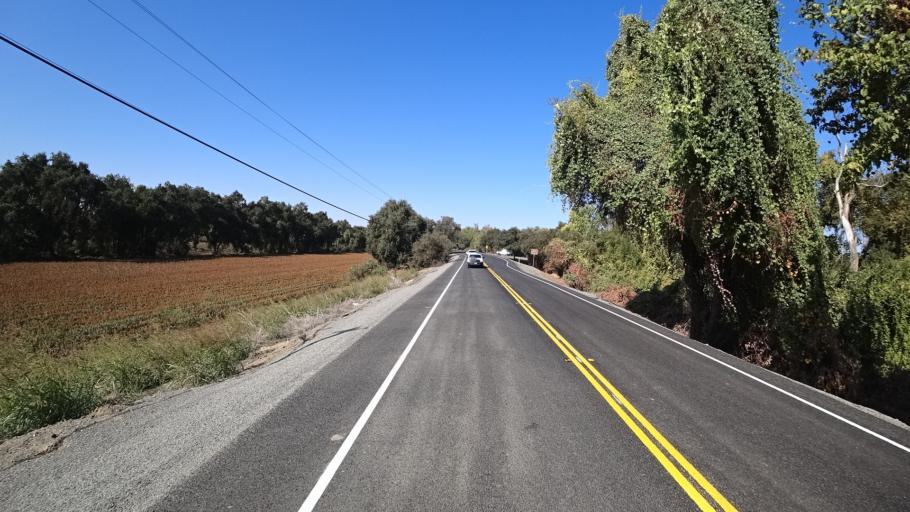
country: US
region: California
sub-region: Yolo County
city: West Sacramento
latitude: 38.6586
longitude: -121.6098
